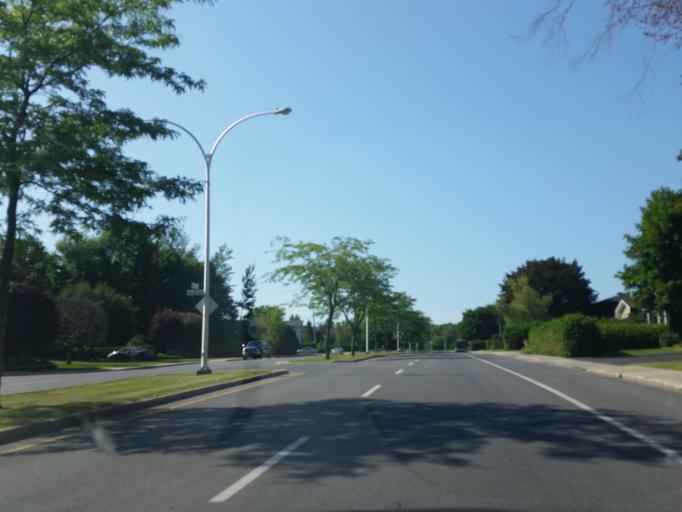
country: CA
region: Quebec
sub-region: Monteregie
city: Saint-Jean-sur-Richelieu
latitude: 45.2940
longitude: -73.2672
